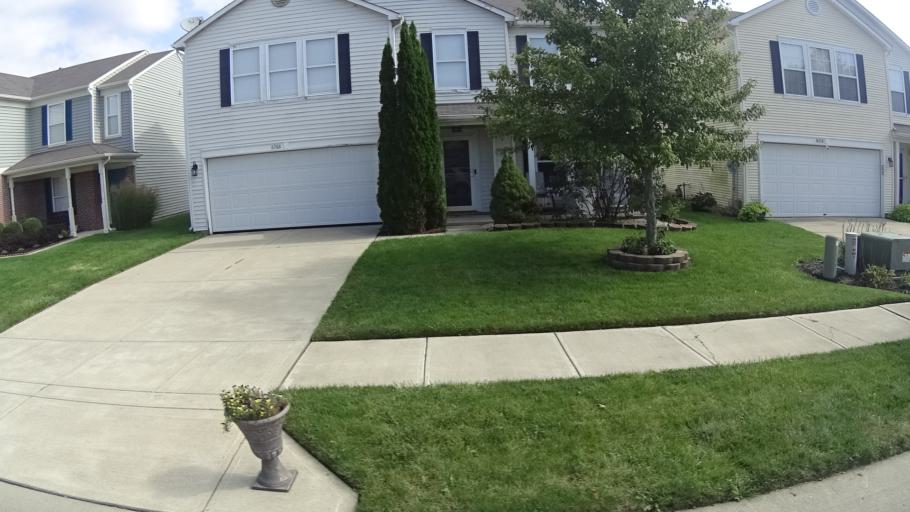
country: US
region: Indiana
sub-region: Hancock County
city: Fortville
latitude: 39.9838
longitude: -85.8500
